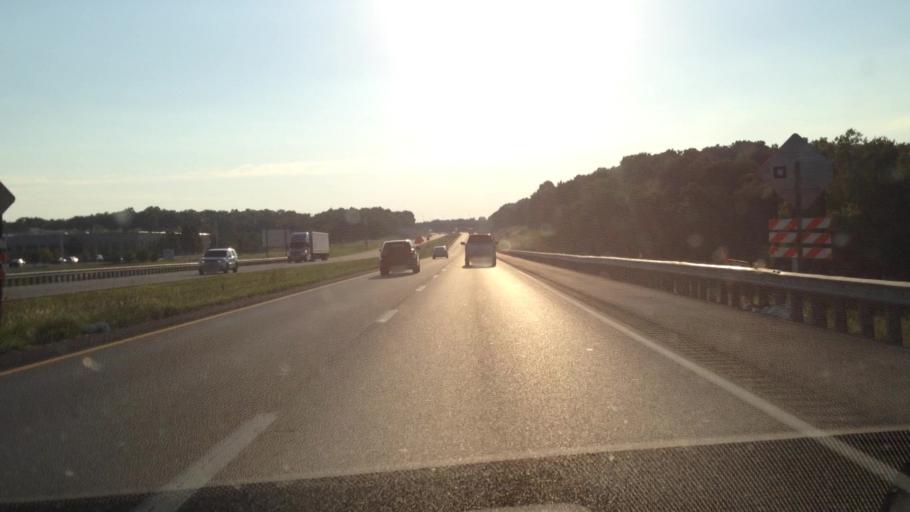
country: US
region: Missouri
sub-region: Jasper County
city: Duquesne
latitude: 37.0463
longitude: -94.4867
